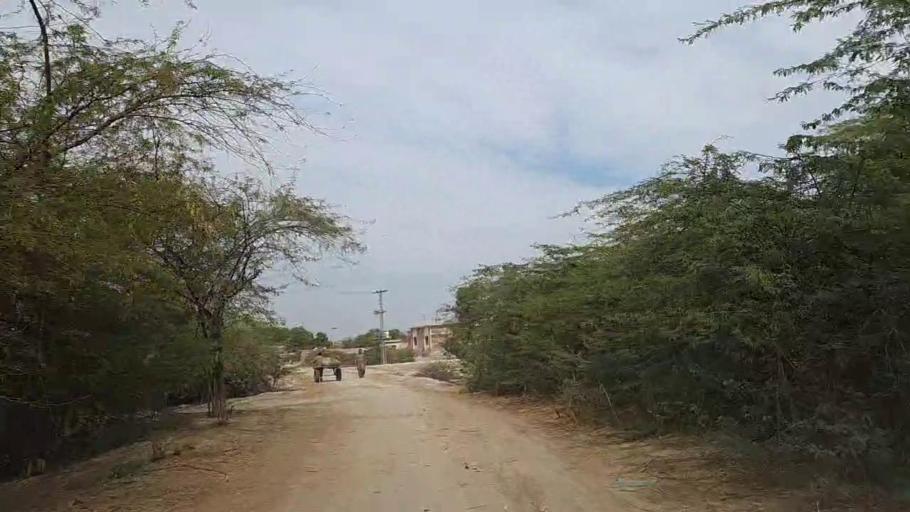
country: PK
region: Sindh
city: Daur
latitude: 26.4250
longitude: 68.4166
